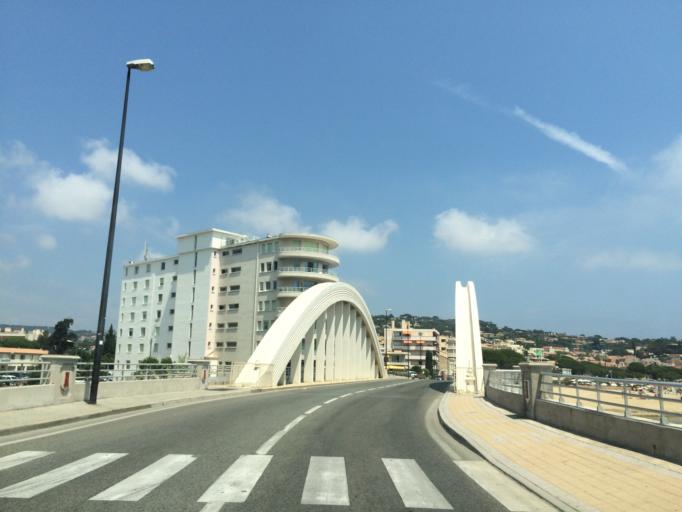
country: FR
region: Provence-Alpes-Cote d'Azur
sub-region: Departement du Var
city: Sainte-Maxime
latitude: 43.3067
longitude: 6.6333
